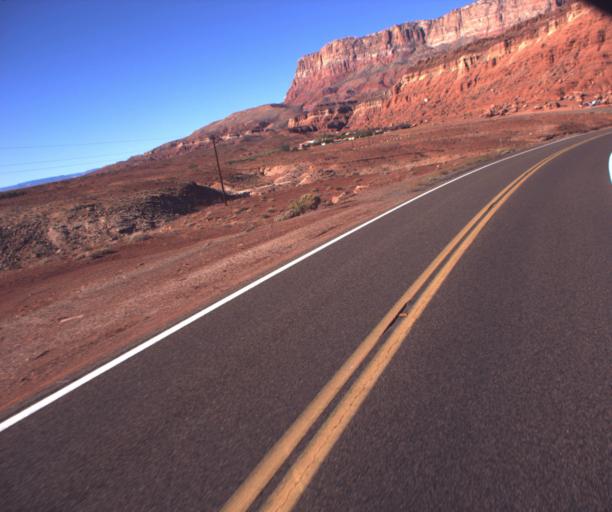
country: US
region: Arizona
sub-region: Coconino County
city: Page
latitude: 36.7464
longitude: -111.7441
